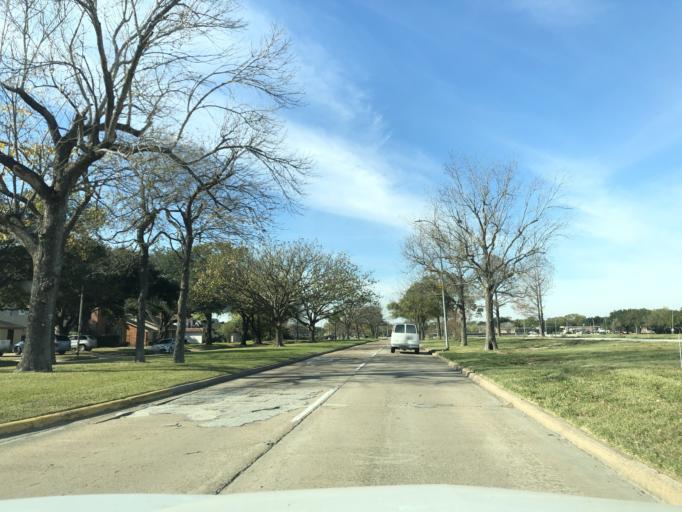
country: US
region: Texas
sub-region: Harris County
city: Bellaire
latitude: 29.6761
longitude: -95.4903
